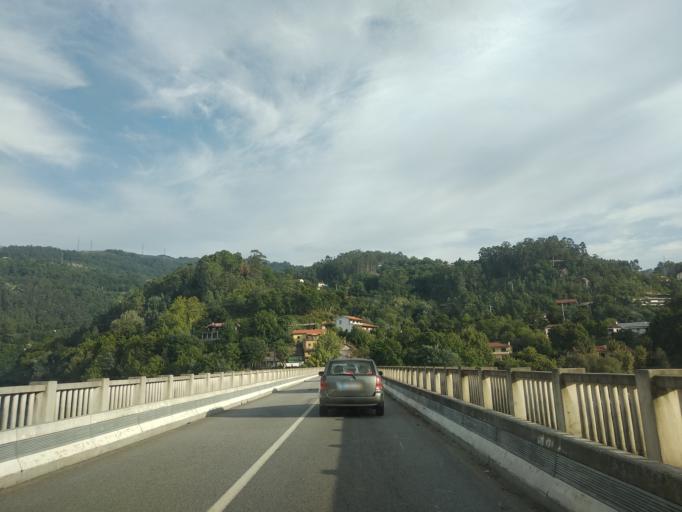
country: PT
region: Braga
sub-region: Vieira do Minho
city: Real
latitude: 41.6753
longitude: -8.1798
